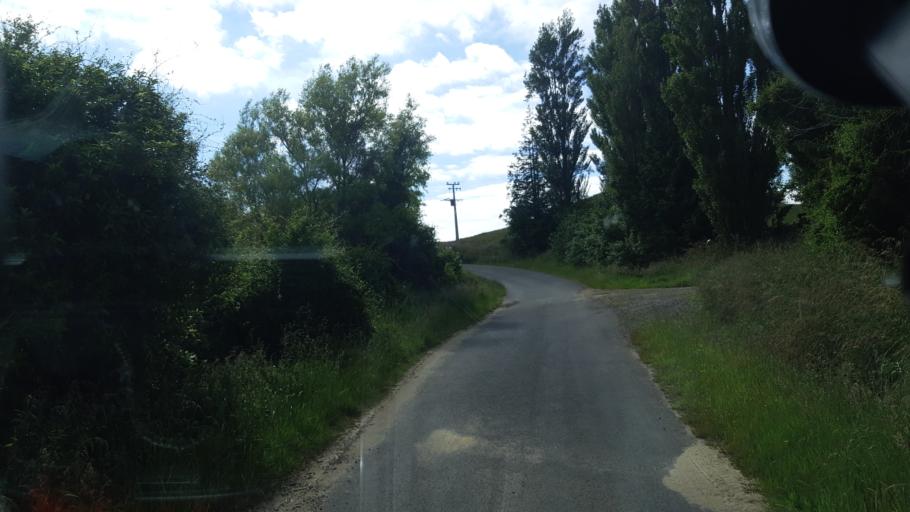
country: NZ
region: Manawatu-Wanganui
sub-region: Rangitikei District
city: Bulls
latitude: -39.9645
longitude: 175.4625
